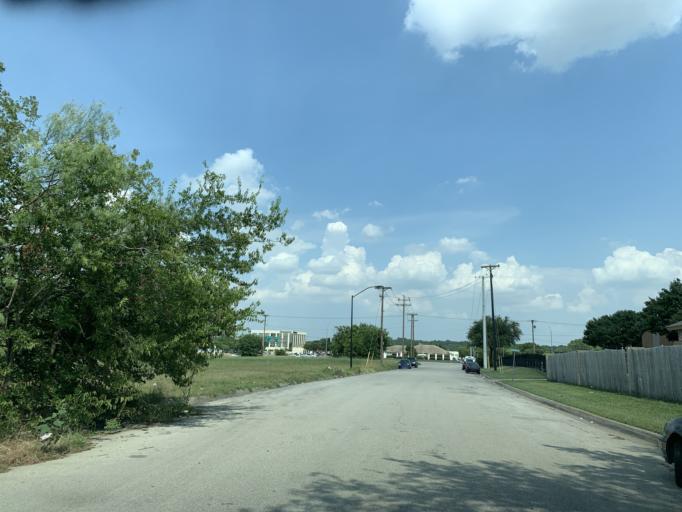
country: US
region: Texas
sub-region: Tarrant County
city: Richland Hills
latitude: 32.7743
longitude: -97.2148
